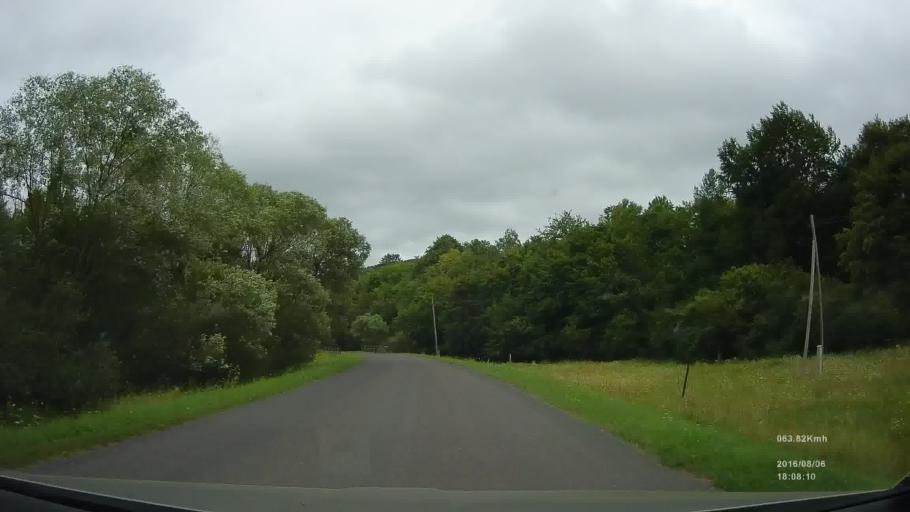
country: SK
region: Presovsky
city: Svidnik
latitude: 49.3892
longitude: 21.5661
